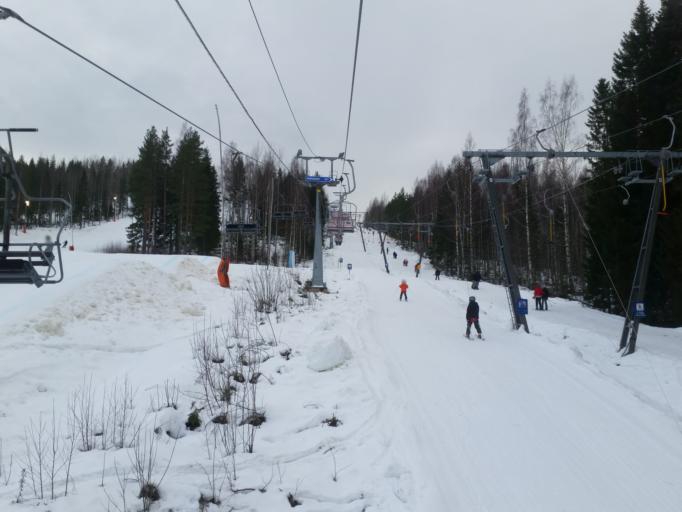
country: SE
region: Gaevleborg
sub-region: Sandvikens Kommun
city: Jarbo
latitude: 60.7560
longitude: 16.4931
